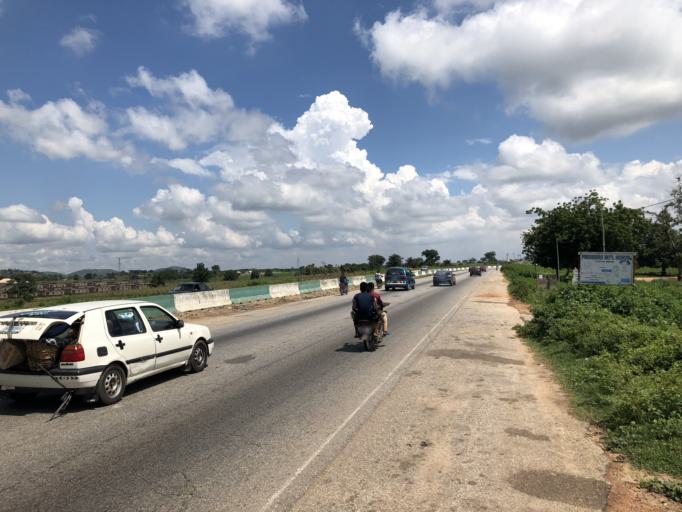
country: NG
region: Nassarawa
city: Karu
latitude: 8.9197
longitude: 7.6930
